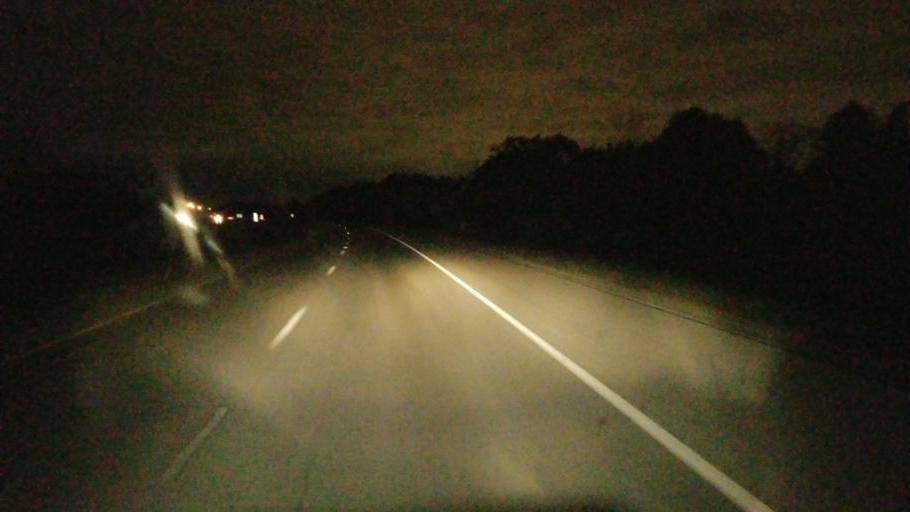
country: US
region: Ohio
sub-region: Franklin County
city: Reynoldsburg
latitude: 39.9505
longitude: -82.7491
